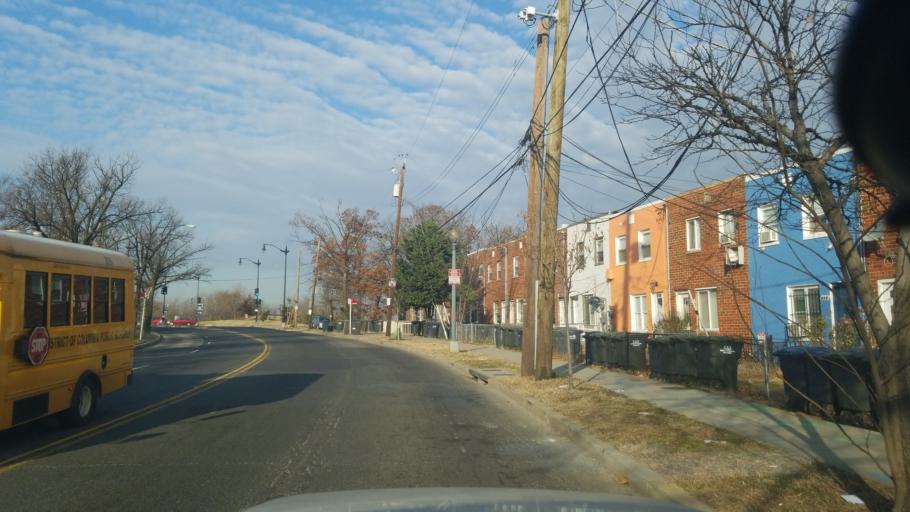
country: US
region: Maryland
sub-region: Prince George's County
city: Mount Rainier
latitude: 38.9122
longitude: -76.9894
